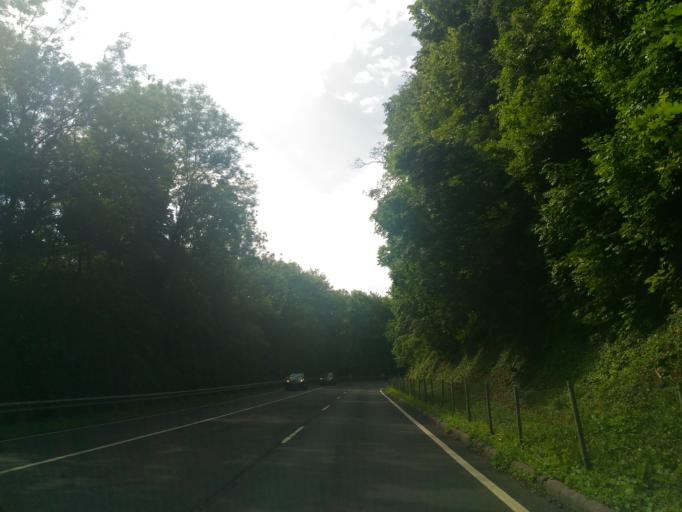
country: HU
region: Baranya
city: Komlo
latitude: 46.1464
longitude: 18.2495
